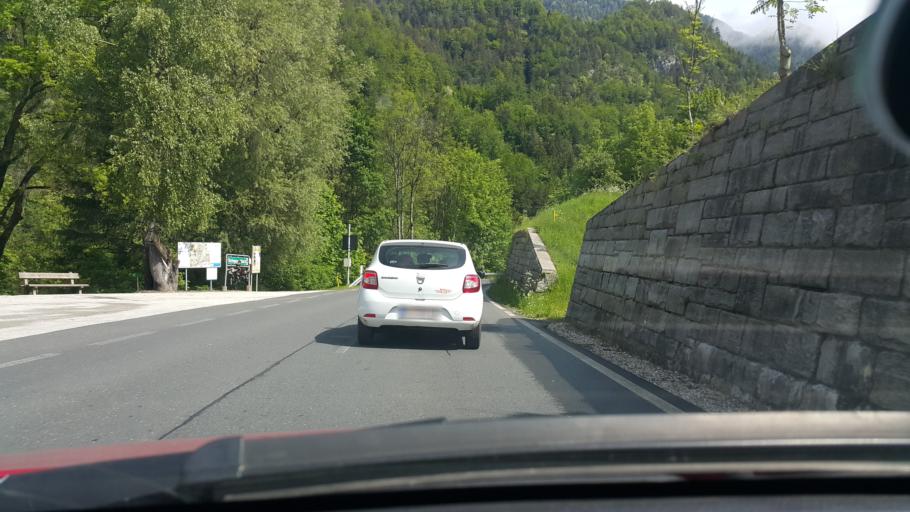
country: AT
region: Carinthia
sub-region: Politischer Bezirk Klagenfurt Land
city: Ferlach
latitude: 46.4786
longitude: 14.2560
